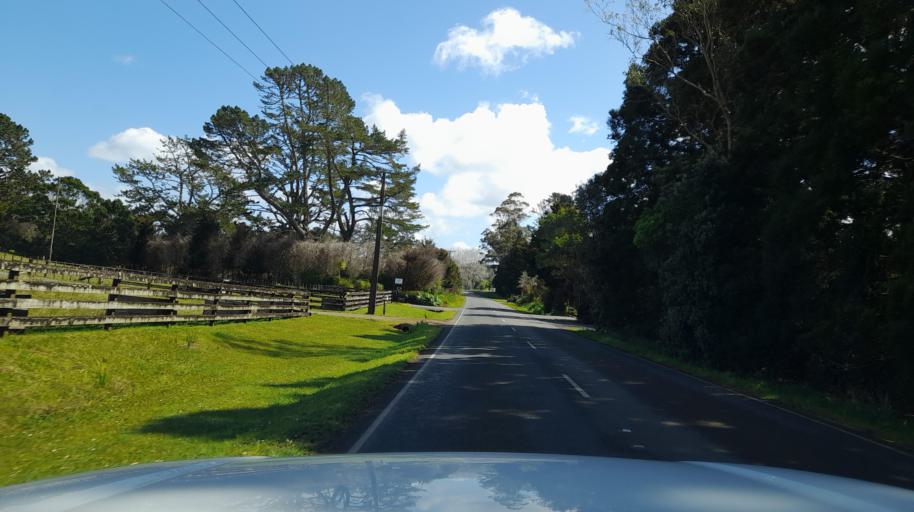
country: NZ
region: Northland
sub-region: Far North District
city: Kerikeri
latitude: -35.2389
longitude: 173.8822
